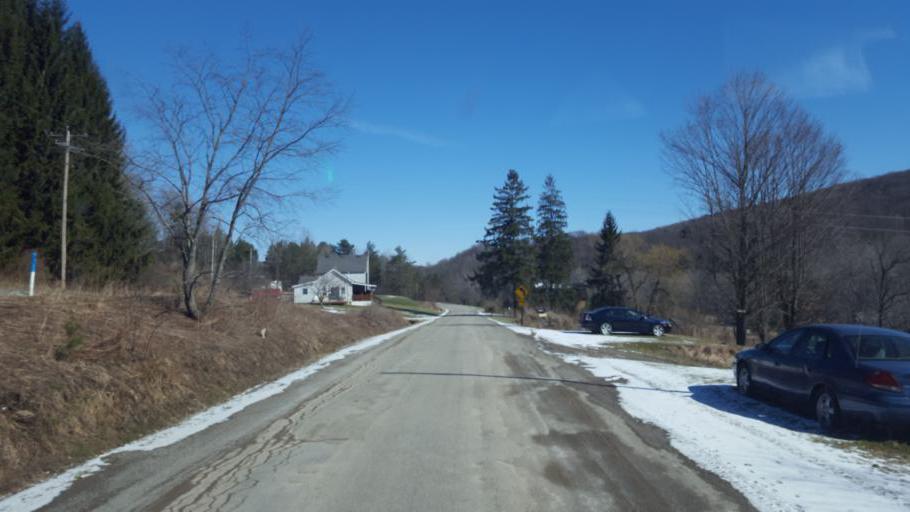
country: US
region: New York
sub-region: Allegany County
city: Wellsville
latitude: 42.0532
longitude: -77.9560
